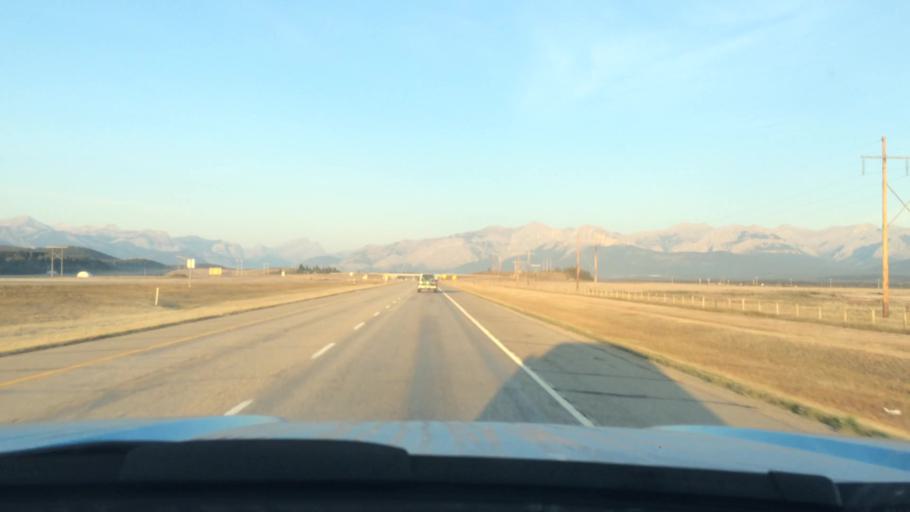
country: CA
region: Alberta
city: Canmore
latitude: 51.1344
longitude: -114.9242
